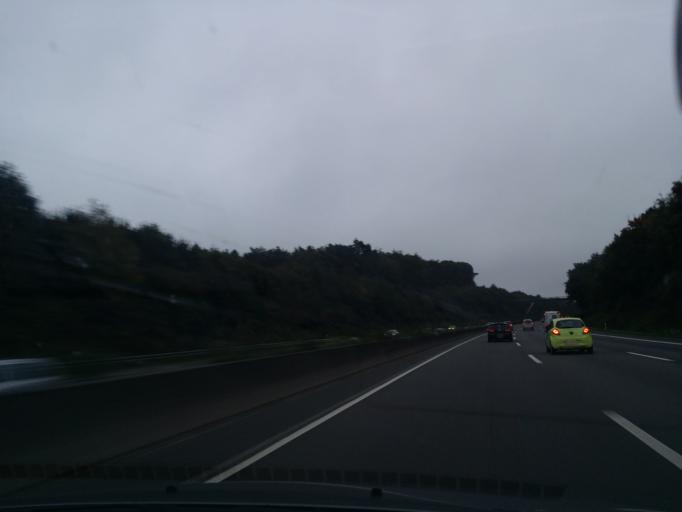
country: DE
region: North Rhine-Westphalia
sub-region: Regierungsbezirk Dusseldorf
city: Remscheid
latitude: 51.2162
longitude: 7.2510
